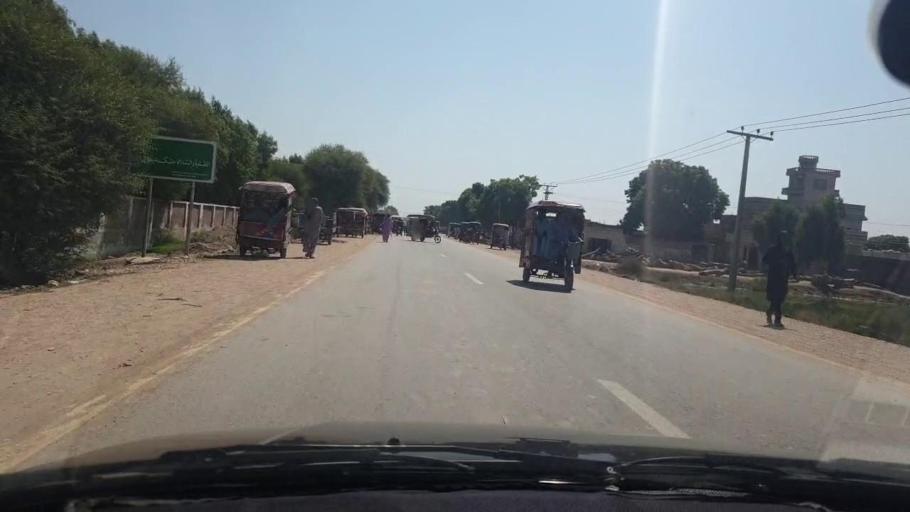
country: PK
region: Sindh
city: Tando Allahyar
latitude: 25.4499
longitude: 68.7270
